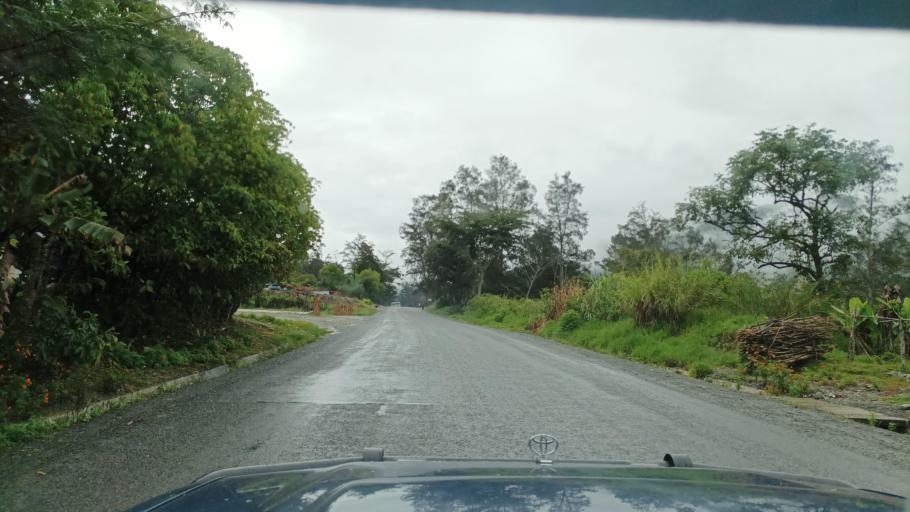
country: PG
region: Western Highlands
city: Rauna
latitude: -5.8332
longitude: 144.3561
